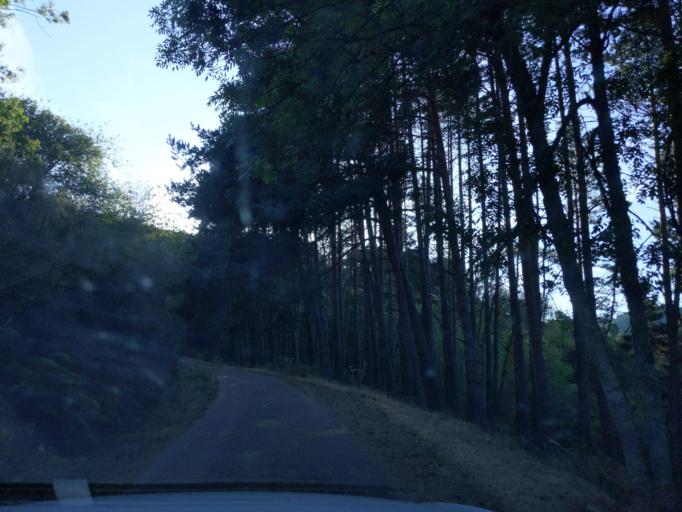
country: ES
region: La Rioja
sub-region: Provincia de La Rioja
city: Ojacastro
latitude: 42.3796
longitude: -3.0173
